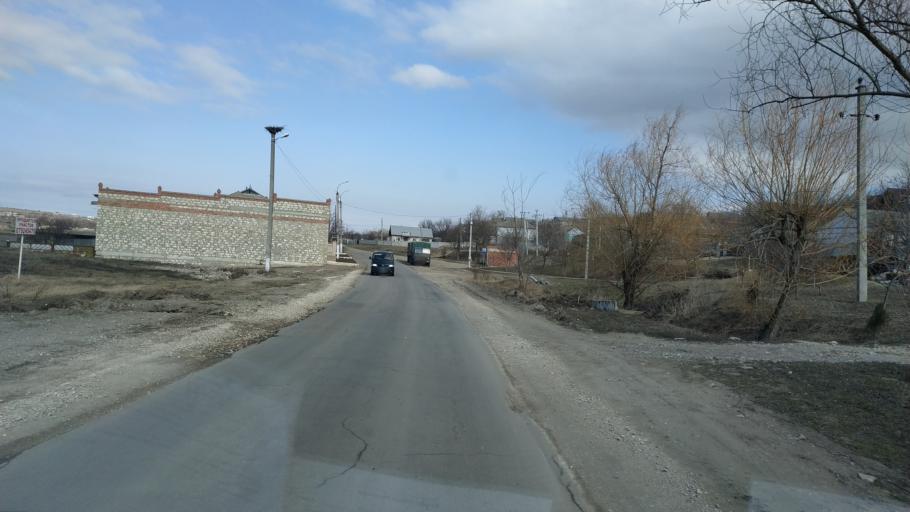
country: MD
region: Causeni
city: Causeni
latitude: 46.6414
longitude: 29.3843
